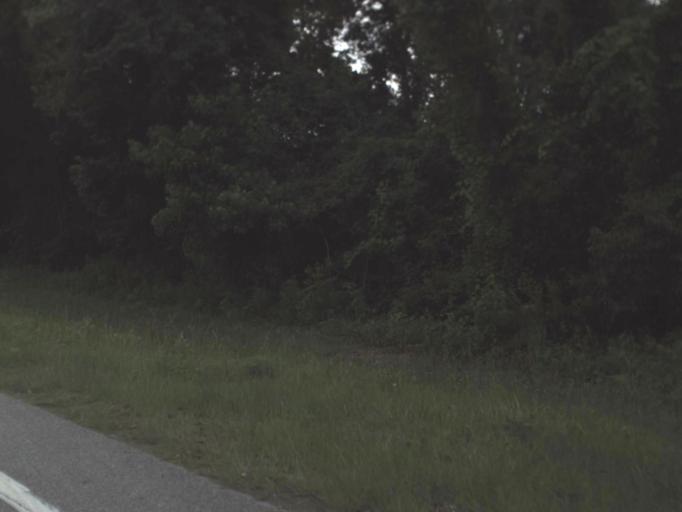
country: US
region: Florida
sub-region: Columbia County
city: Watertown
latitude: 30.1771
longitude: -82.5904
